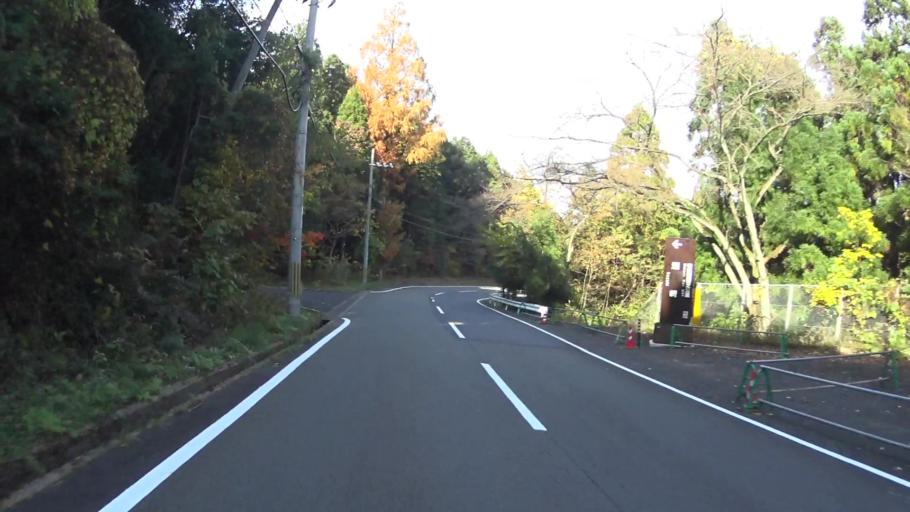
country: JP
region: Kyoto
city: Maizuru
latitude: 35.5463
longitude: 135.3958
